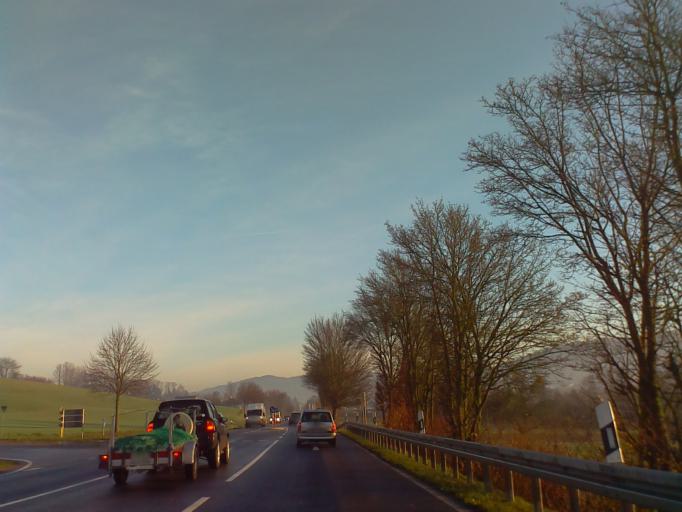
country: DE
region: Hesse
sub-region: Regierungsbezirk Darmstadt
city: Rimbach
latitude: 49.6423
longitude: 8.7665
